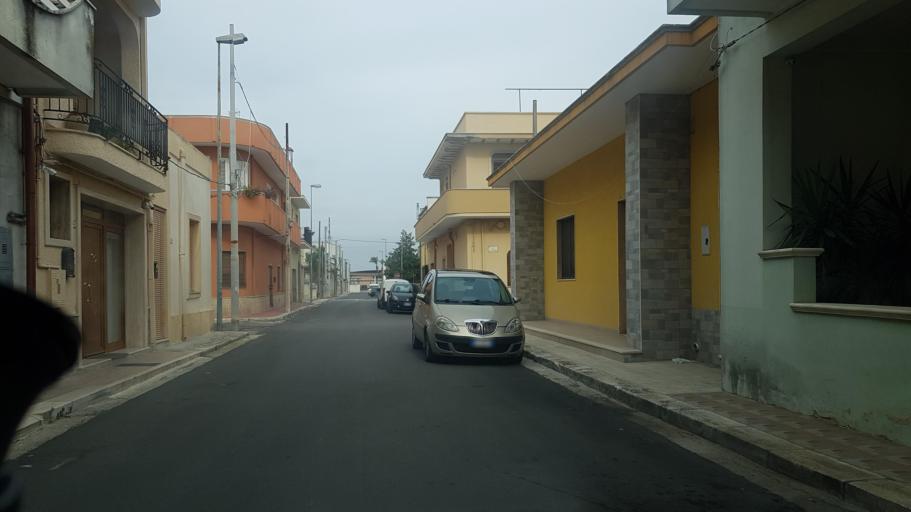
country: IT
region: Apulia
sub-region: Provincia di Brindisi
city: Cellino San Marco
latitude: 40.4748
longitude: 17.9645
